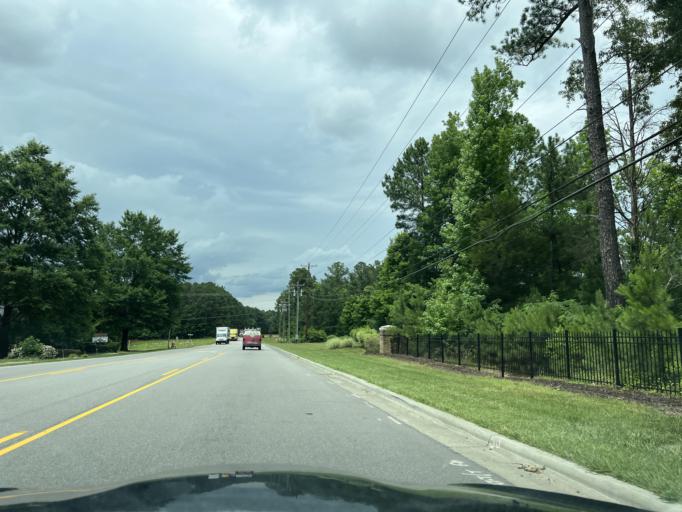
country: US
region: North Carolina
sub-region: Wake County
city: Morrisville
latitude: 35.9108
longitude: -78.8166
